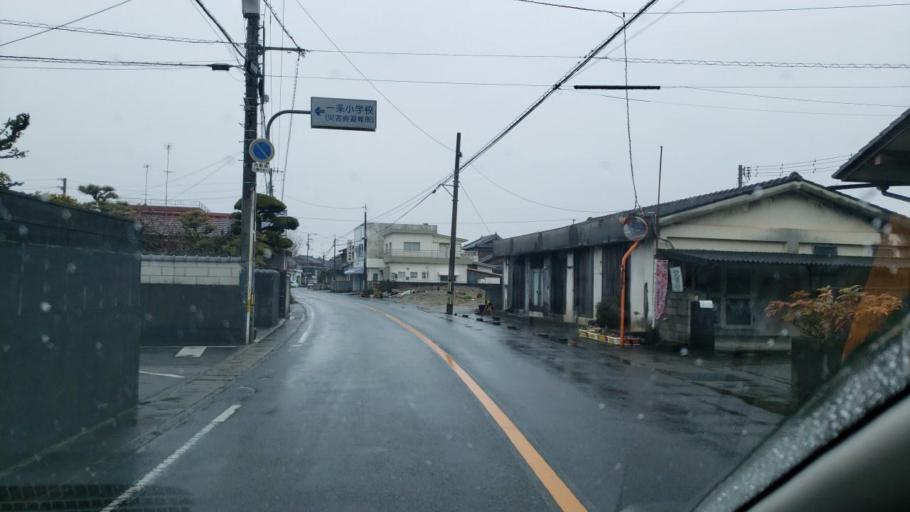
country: JP
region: Tokushima
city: Kamojimacho-jogejima
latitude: 34.0994
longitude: 134.3873
